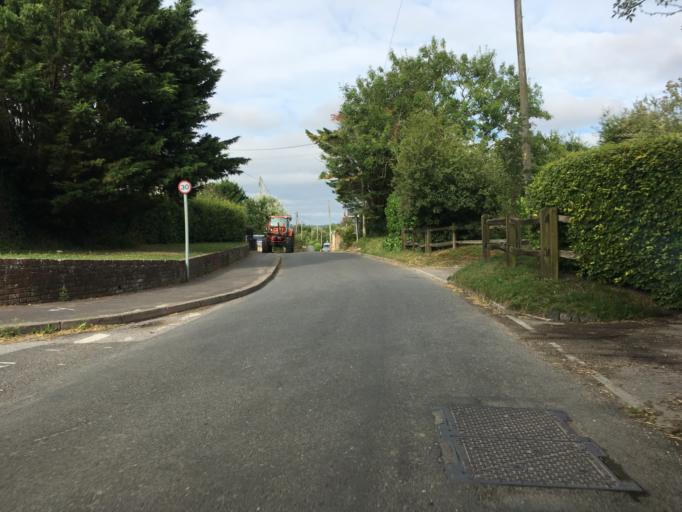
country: GB
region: England
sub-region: Hampshire
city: Colden Common
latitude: 51.0094
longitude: -1.2654
